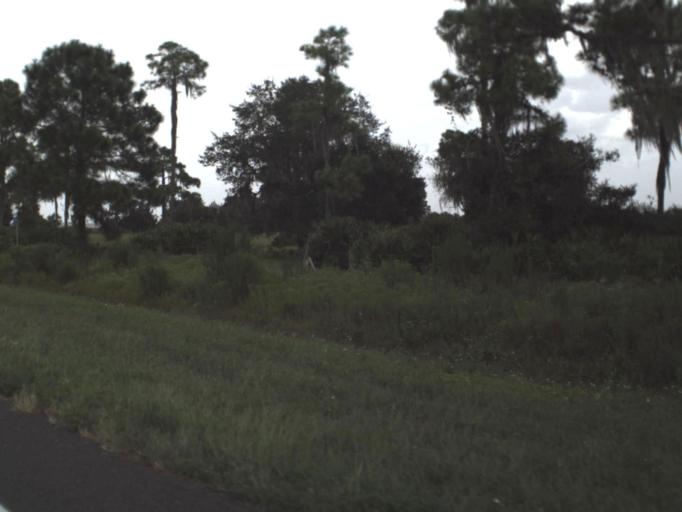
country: US
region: Florida
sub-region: Polk County
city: Crooked Lake Park
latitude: 27.7861
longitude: -81.5971
